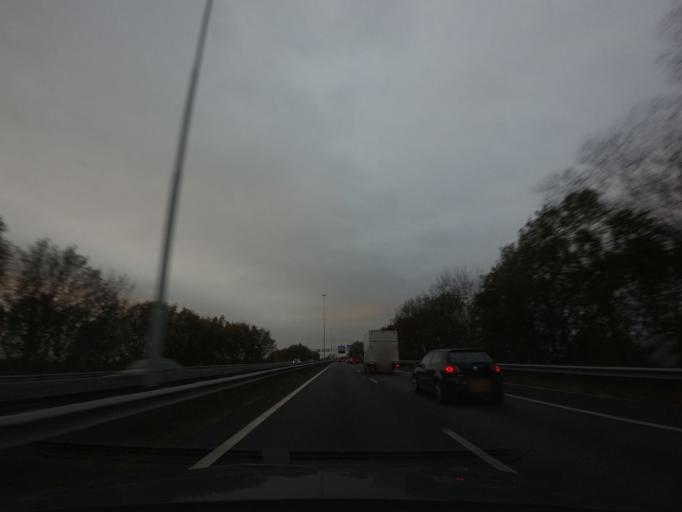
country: NL
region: North Brabant
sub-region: Gemeente Breda
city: Hoge Vucht
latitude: 51.5980
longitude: 4.8355
